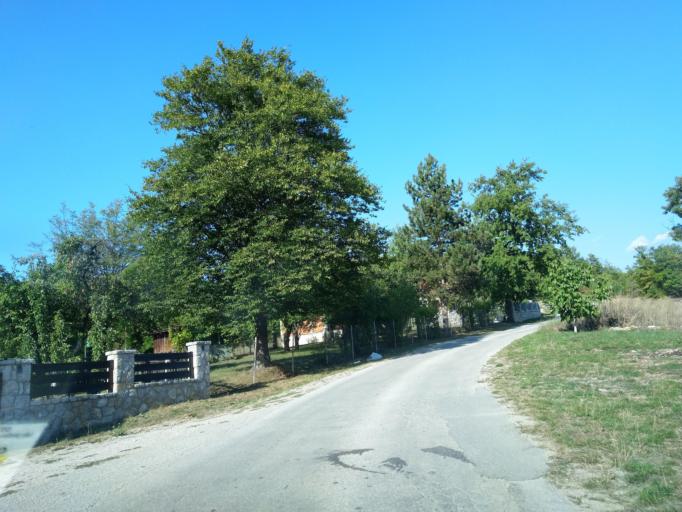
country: RS
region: Central Serbia
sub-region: Zlatiborski Okrug
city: Uzice
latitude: 43.8118
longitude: 19.8483
